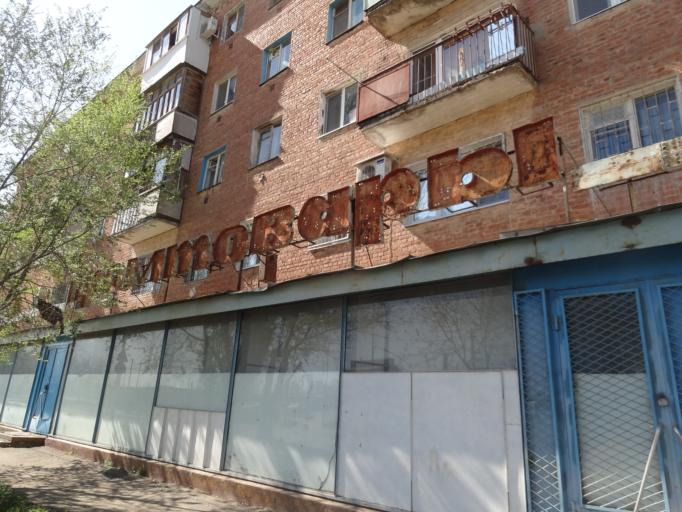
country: RU
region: Saratov
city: Engel's
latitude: 51.4690
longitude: 46.1479
